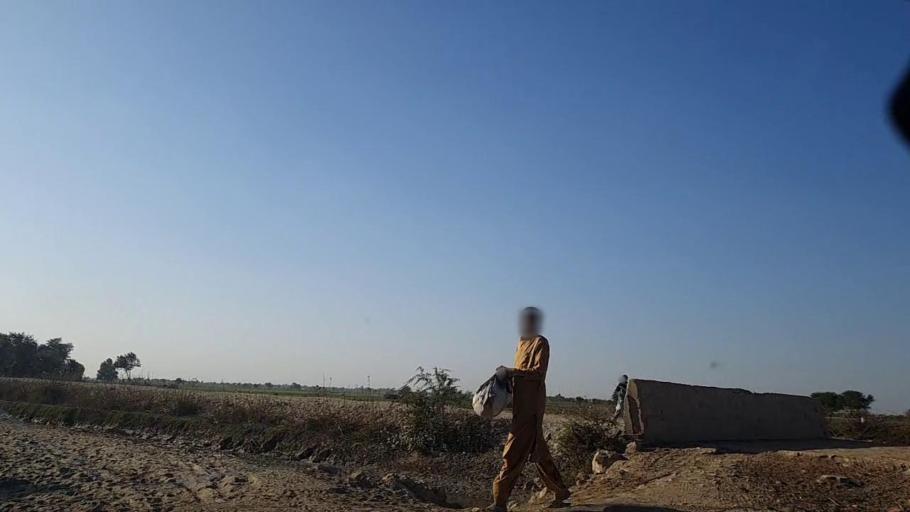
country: PK
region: Sindh
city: Khanpur
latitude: 27.7722
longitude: 69.2897
